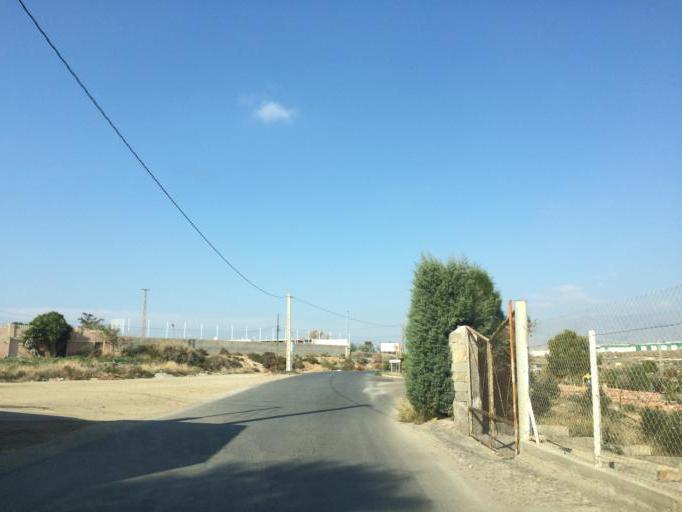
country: ES
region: Andalusia
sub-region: Provincia de Almeria
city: Viator
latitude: 36.8674
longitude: -2.4189
